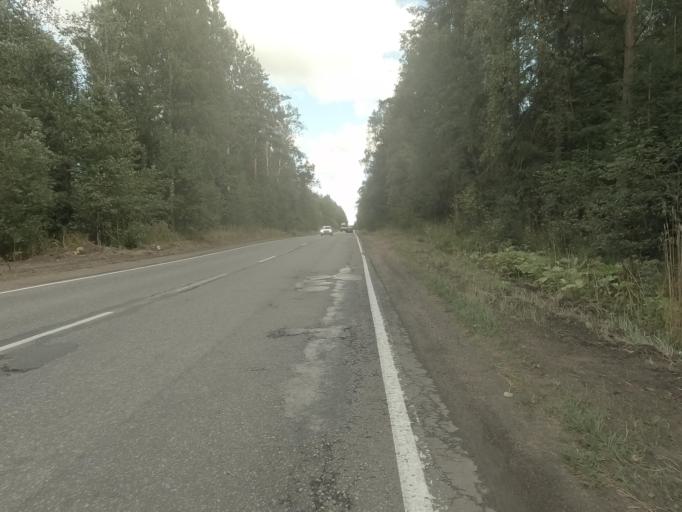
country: RU
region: Leningrad
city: Shcheglovo
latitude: 60.0205
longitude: 30.7318
